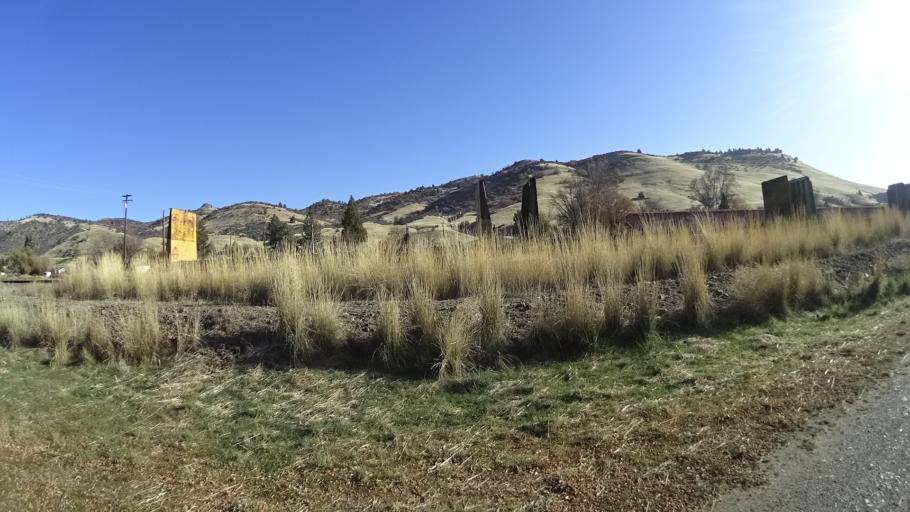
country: US
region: California
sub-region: Siskiyou County
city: Montague
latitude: 41.9085
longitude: -122.5543
